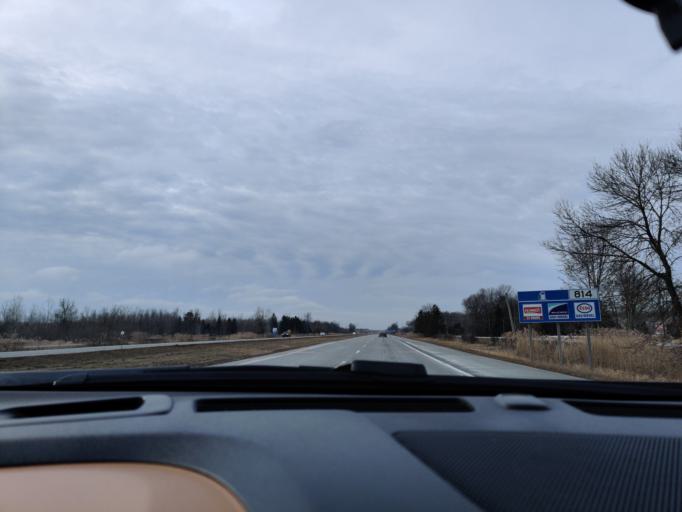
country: CA
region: Quebec
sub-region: Monteregie
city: Les Coteaux
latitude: 45.1688
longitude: -74.4289
